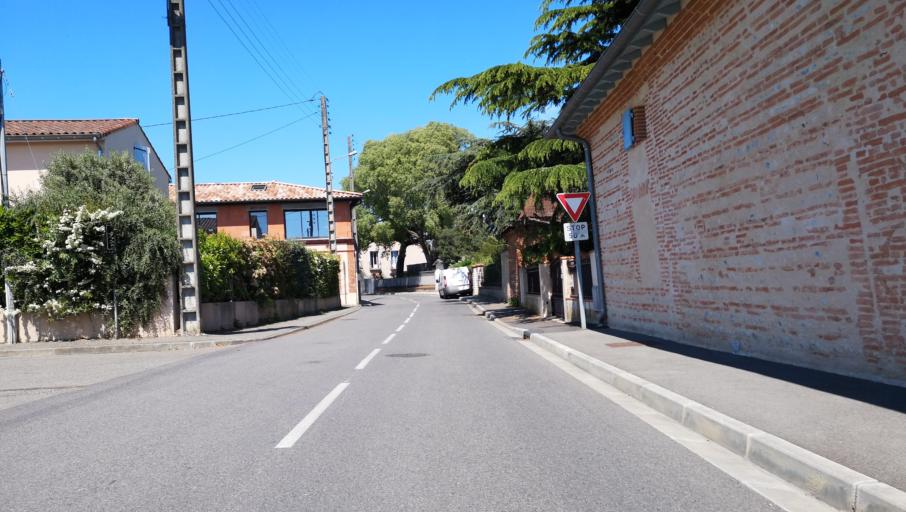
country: FR
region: Midi-Pyrenees
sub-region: Departement de la Haute-Garonne
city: Blagnac
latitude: 43.6401
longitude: 1.3912
